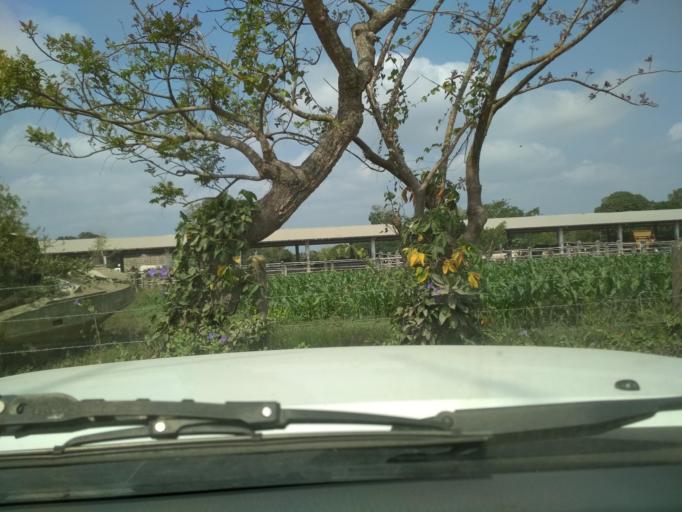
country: MX
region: Veracruz
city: El Tejar
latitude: 19.0864
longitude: -96.1707
